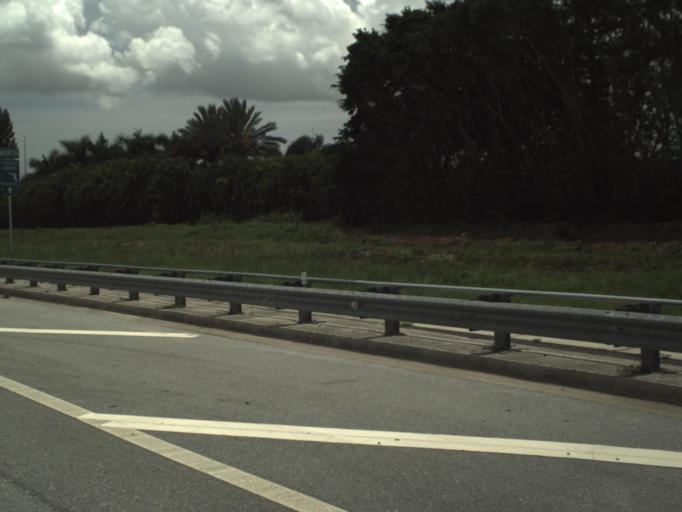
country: US
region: Florida
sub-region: Palm Beach County
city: Villages of Oriole
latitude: 26.4537
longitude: -80.1771
